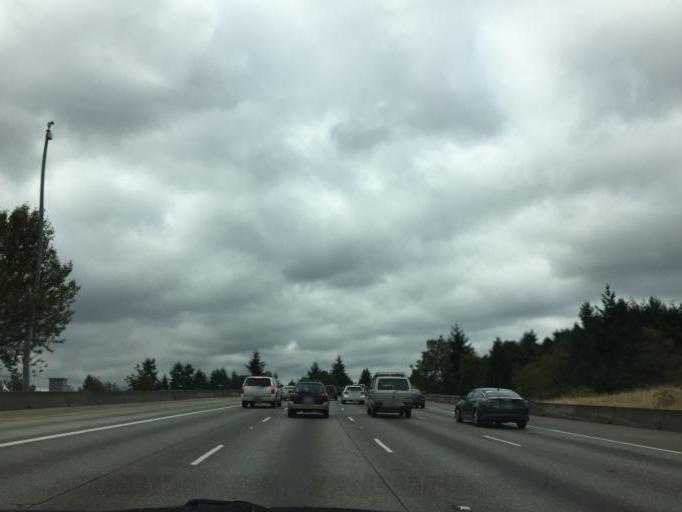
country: US
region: Washington
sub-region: King County
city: SeaTac
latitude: 47.4323
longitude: -122.2712
